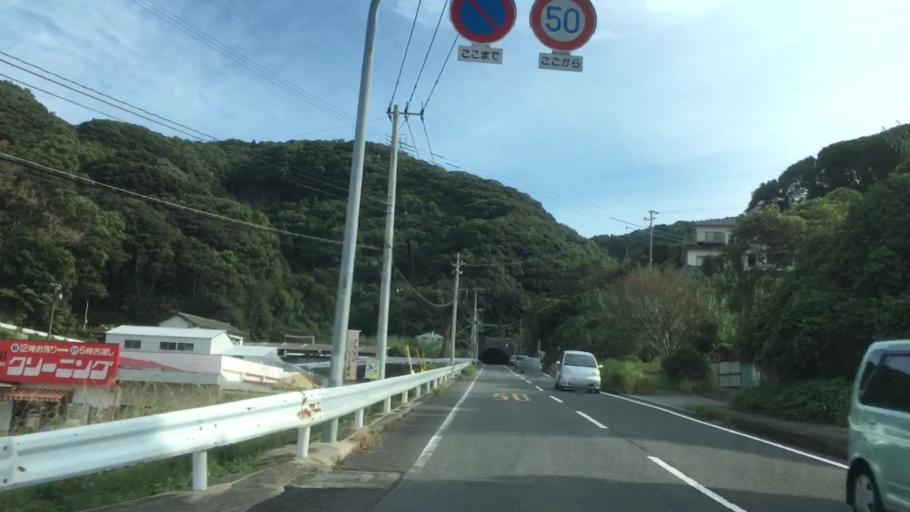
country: JP
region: Nagasaki
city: Sasebo
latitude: 32.9480
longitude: 129.6390
